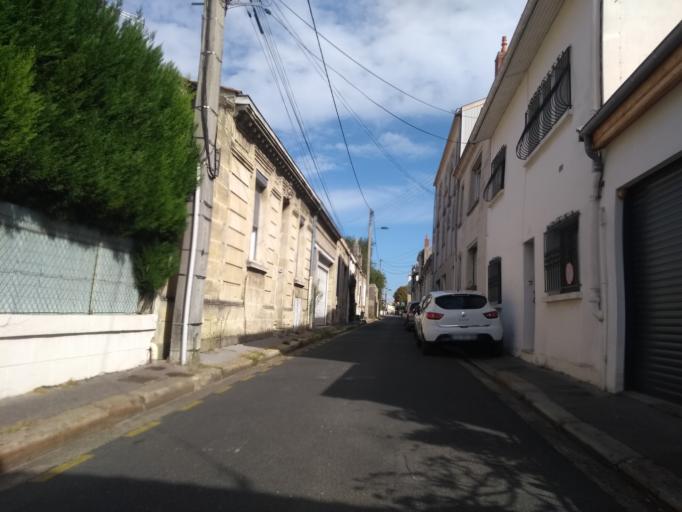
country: FR
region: Aquitaine
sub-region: Departement de la Gironde
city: Merignac
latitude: 44.8316
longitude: -0.6106
